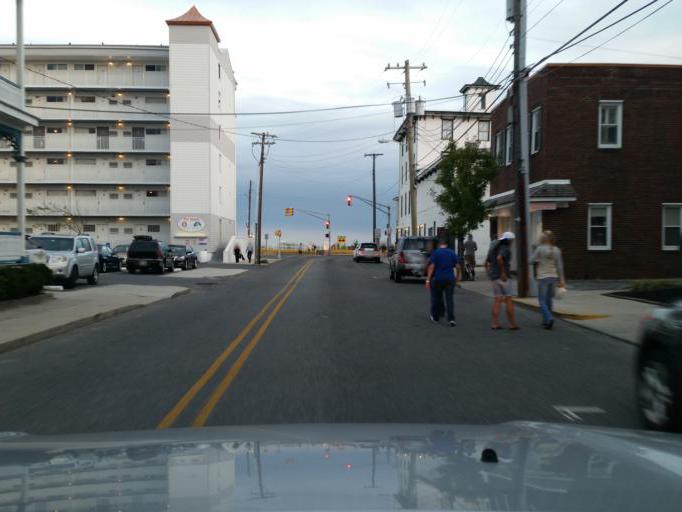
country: US
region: New Jersey
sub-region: Cape May County
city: Cape May
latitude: 38.9311
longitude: -74.9213
